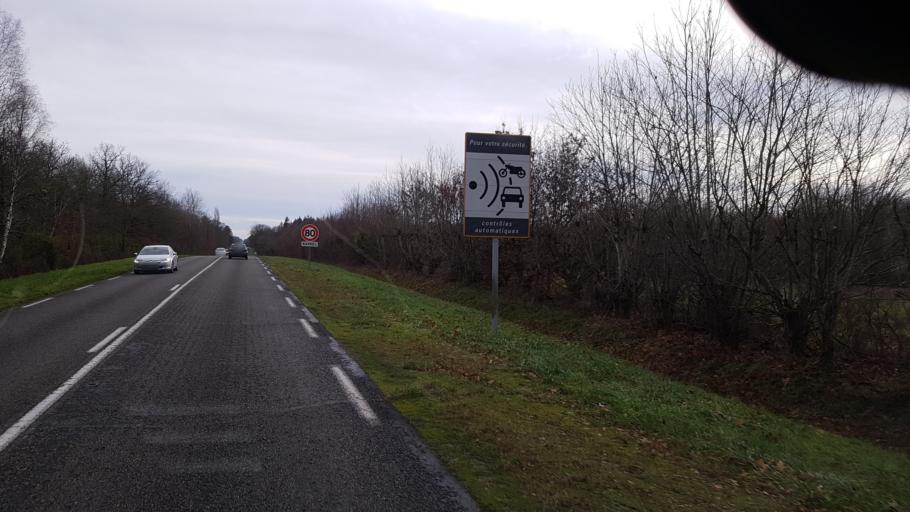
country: FR
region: Centre
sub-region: Departement du Loiret
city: La Ferte-Saint-Aubin
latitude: 47.6918
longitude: 1.9559
